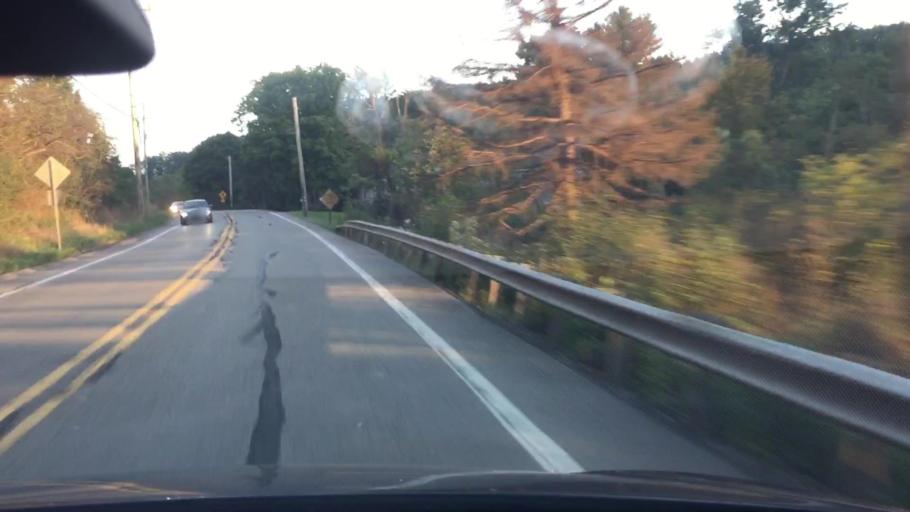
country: US
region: Pennsylvania
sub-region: Allegheny County
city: Curtisville
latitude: 40.6105
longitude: -79.8944
